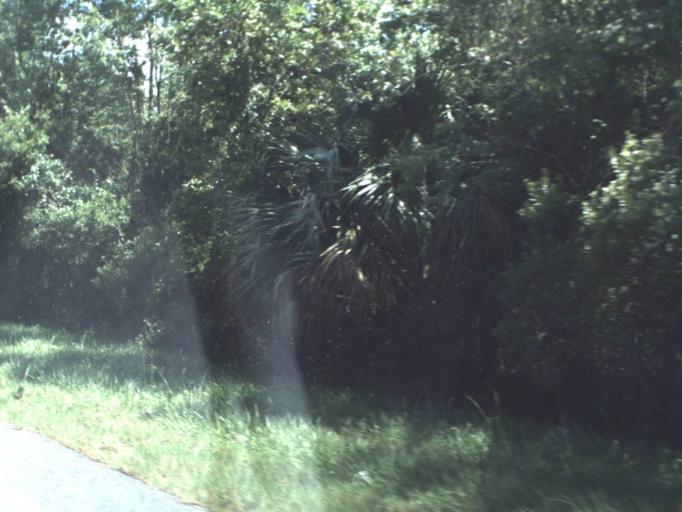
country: US
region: Florida
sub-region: Nassau County
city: Yulee
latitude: 30.6549
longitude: -81.6278
